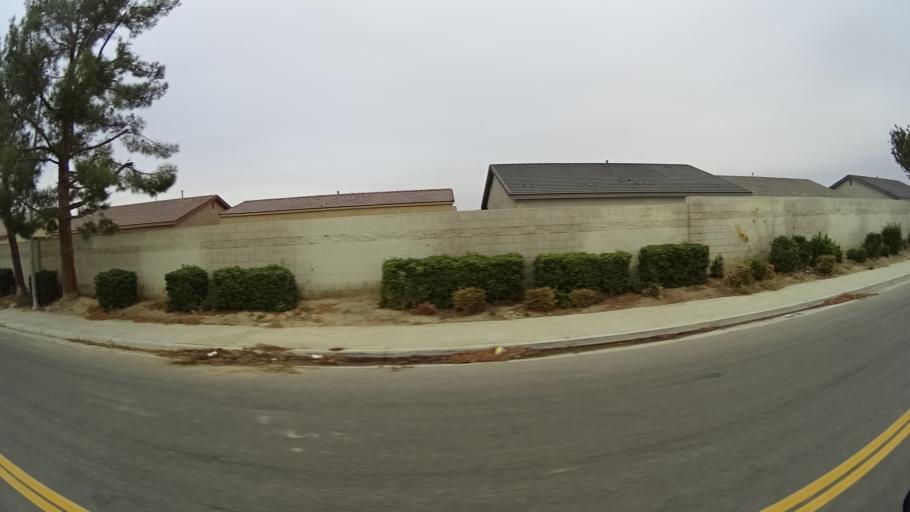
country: US
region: California
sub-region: Kern County
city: Bakersfield
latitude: 35.3397
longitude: -118.9426
